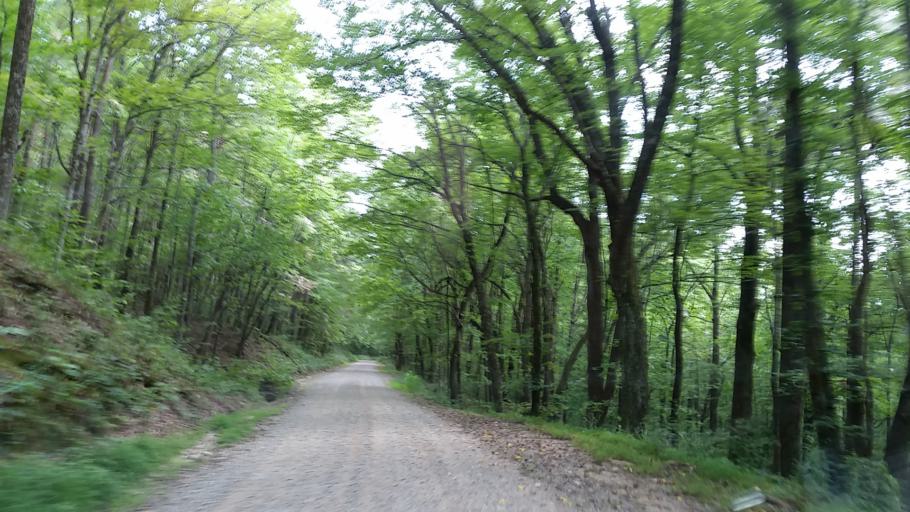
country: US
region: Georgia
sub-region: Lumpkin County
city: Dahlonega
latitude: 34.6465
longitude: -84.0536
